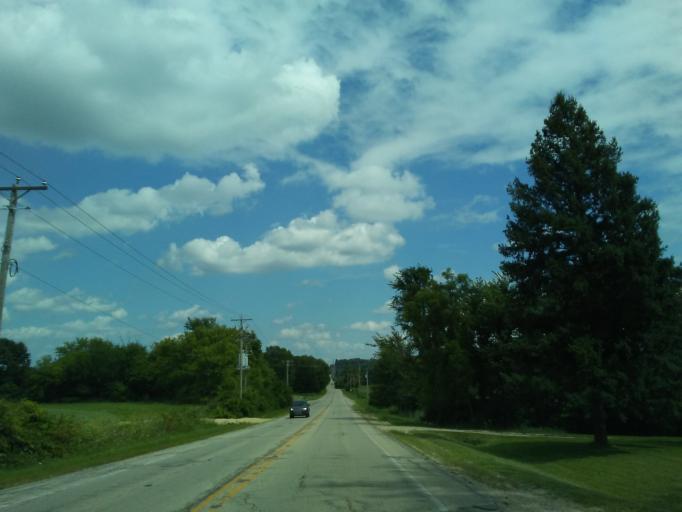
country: US
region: Wisconsin
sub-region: Dane County
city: Verona
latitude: 43.0162
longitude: -89.5452
